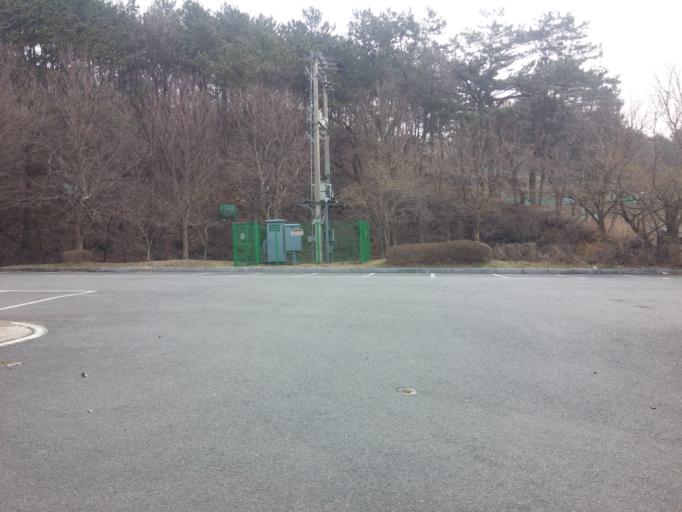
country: KR
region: Ulsan
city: Ulsan
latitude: 35.5874
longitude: 129.4562
